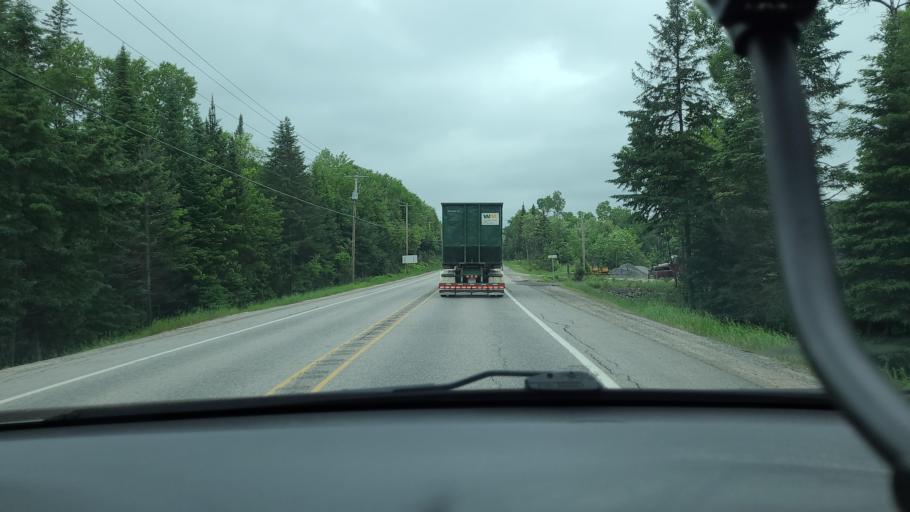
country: CA
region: Quebec
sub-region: Laurentides
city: Labelle
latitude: 46.3001
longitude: -74.7812
